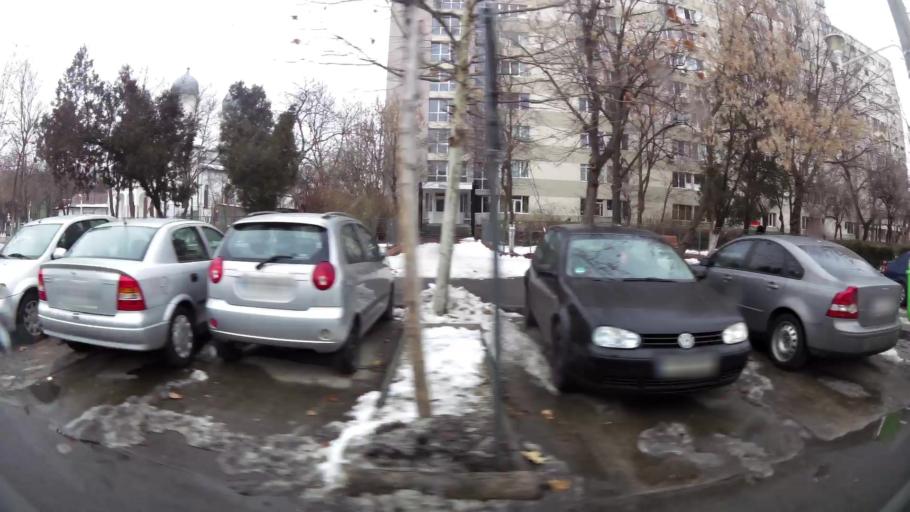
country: RO
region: Ilfov
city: Dobroesti
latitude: 44.4195
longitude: 26.1650
